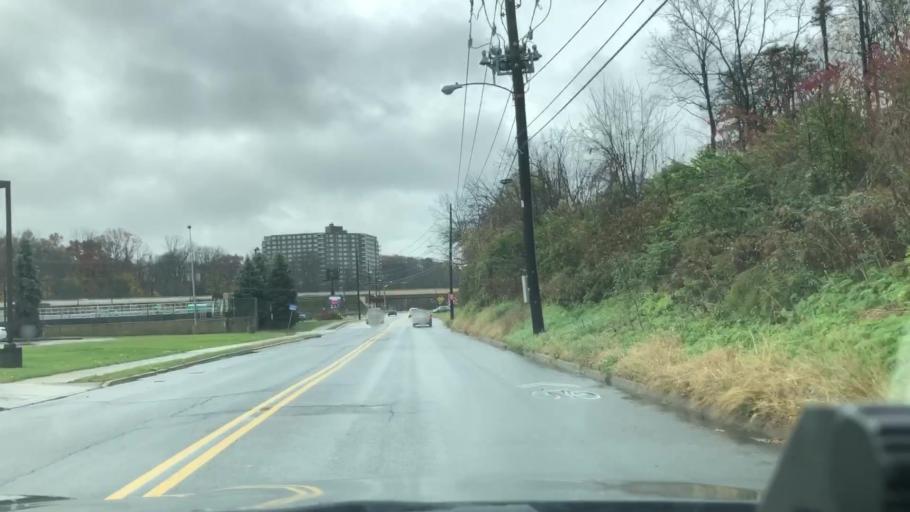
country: US
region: Pennsylvania
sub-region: Lehigh County
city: Allentown
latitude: 40.5938
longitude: -75.4822
